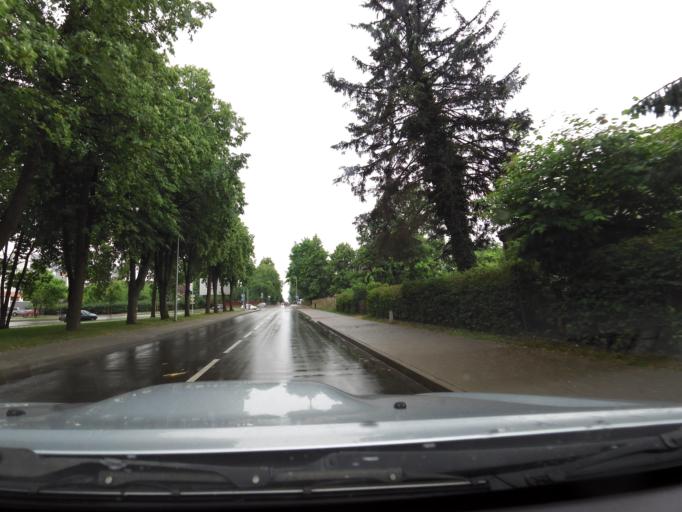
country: LT
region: Marijampoles apskritis
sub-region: Marijampole Municipality
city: Marijampole
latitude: 54.5481
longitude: 23.3469
